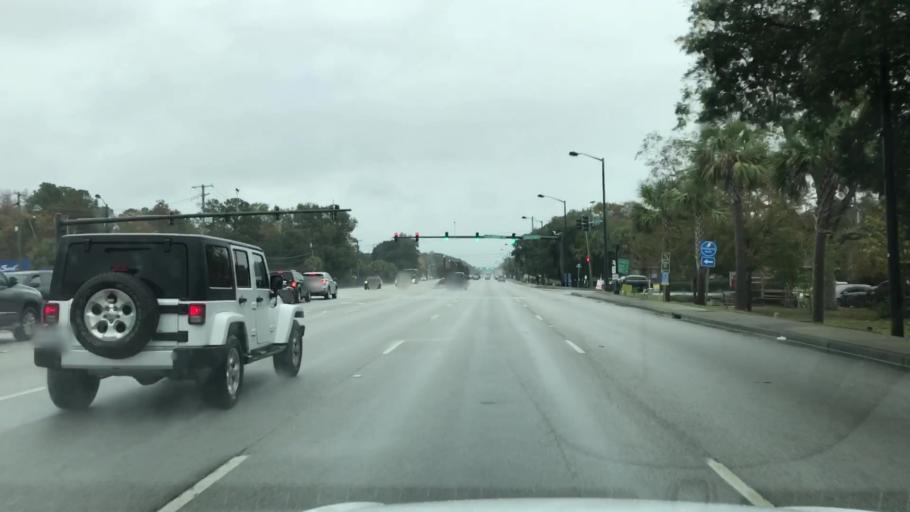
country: US
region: South Carolina
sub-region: Charleston County
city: Isle of Palms
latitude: 32.8585
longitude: -79.7957
